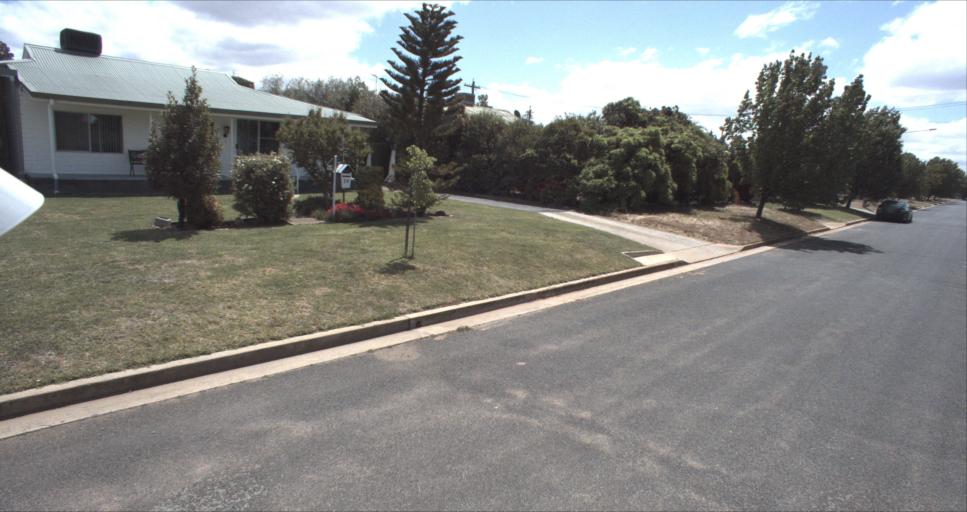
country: AU
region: New South Wales
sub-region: Leeton
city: Leeton
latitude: -34.5610
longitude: 146.3986
